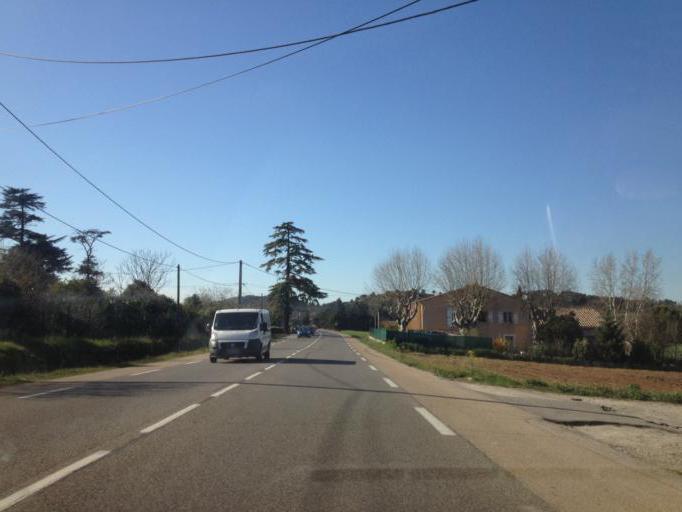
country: FR
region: Provence-Alpes-Cote d'Azur
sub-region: Departement des Bouches-du-Rhone
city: Bouc-Bel-Air
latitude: 43.5019
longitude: 5.4000
